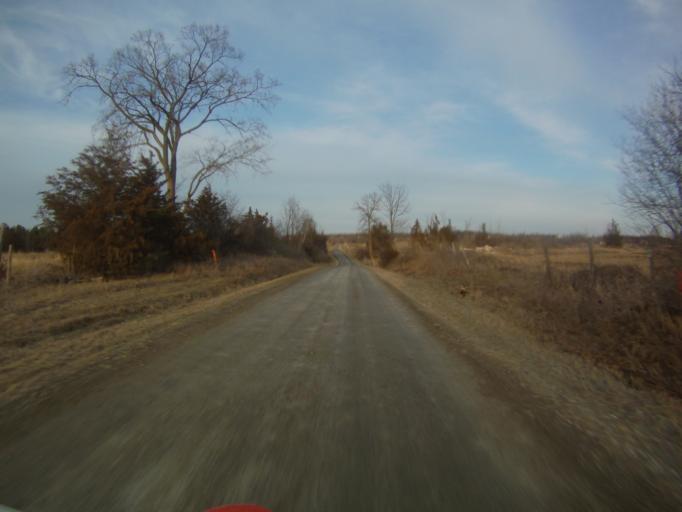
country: US
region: Vermont
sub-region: Addison County
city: Vergennes
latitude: 44.1323
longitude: -73.3043
